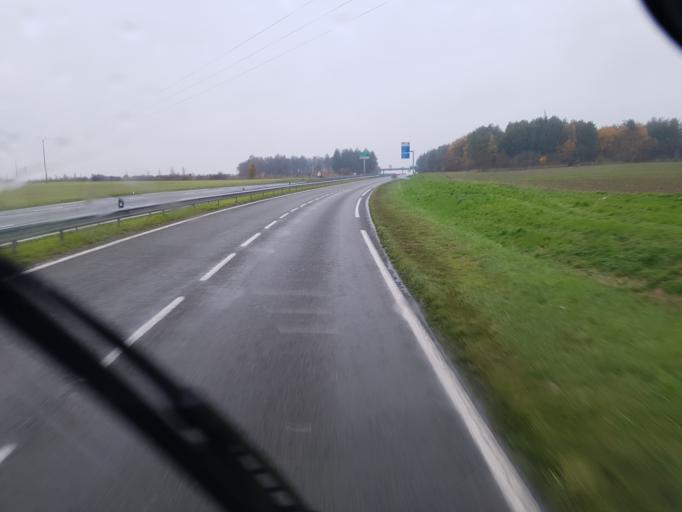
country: FR
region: Picardie
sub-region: Departement de l'Aisne
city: Gauchy
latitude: 49.8107
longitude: 3.2873
